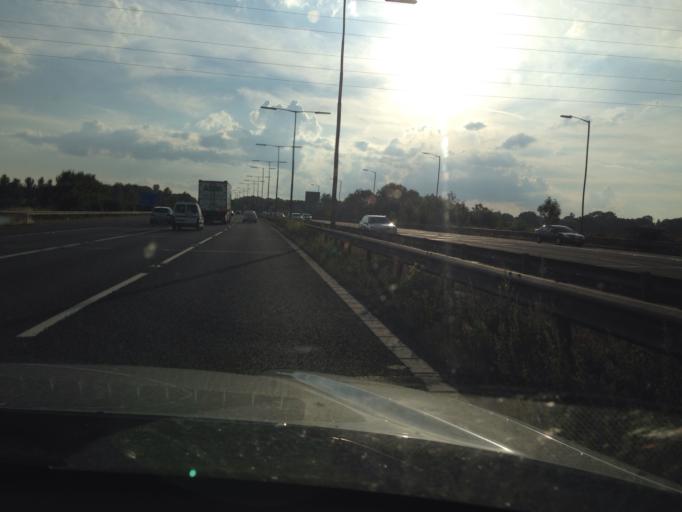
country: GB
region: England
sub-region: Buckinghamshire
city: Denham
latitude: 51.5617
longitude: -0.5065
